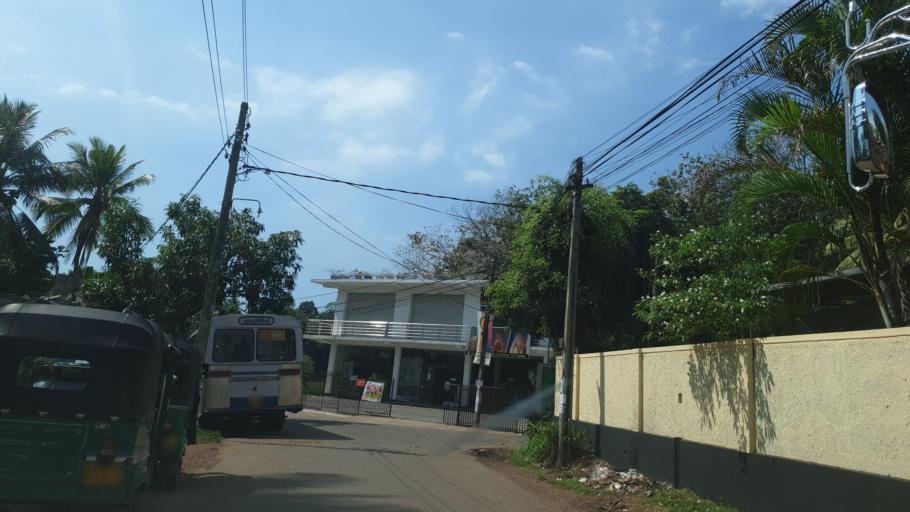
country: LK
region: Western
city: Panadura
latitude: 6.7226
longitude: 79.9597
